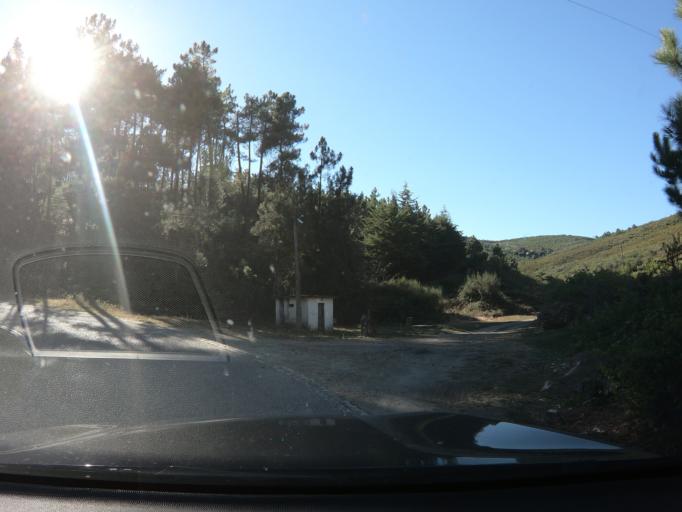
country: PT
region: Vila Real
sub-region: Sabrosa
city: Vilela
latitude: 41.2251
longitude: -7.5825
